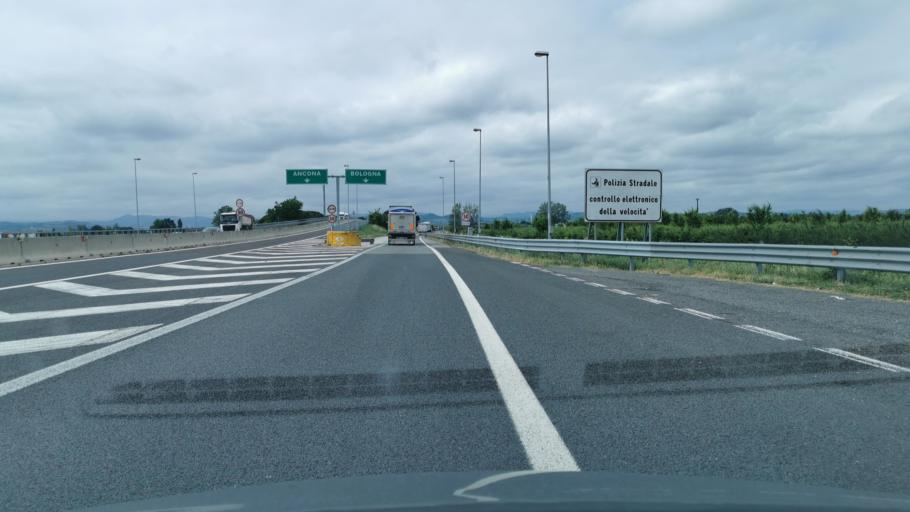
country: IT
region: Emilia-Romagna
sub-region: Provincia di Ravenna
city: Solarolo
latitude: 44.3570
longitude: 11.8191
